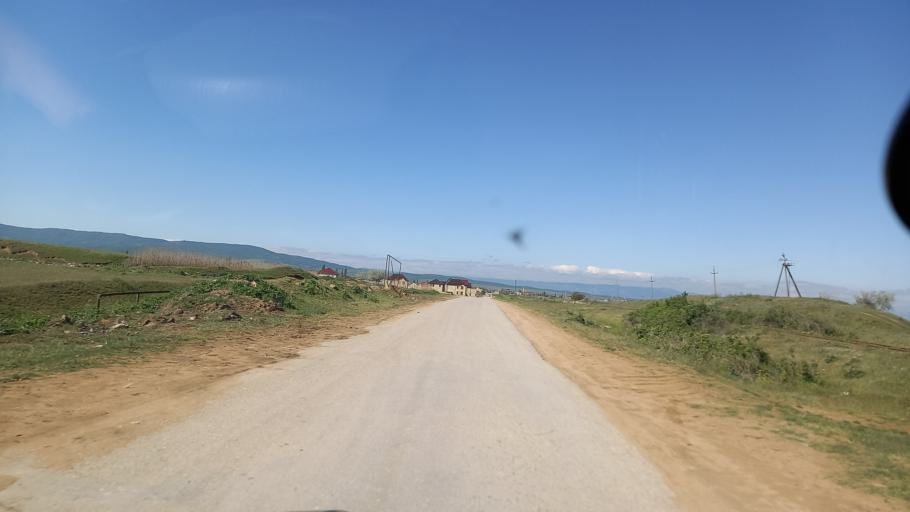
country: RU
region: Dagestan
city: Dagestanskiye Ogni
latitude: 42.1312
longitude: 48.2274
